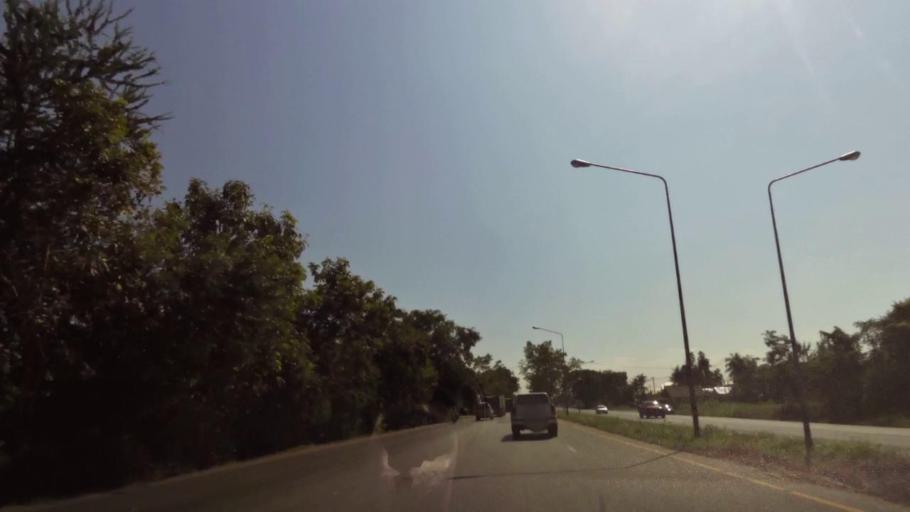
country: TH
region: Nakhon Sawan
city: Kao Liao
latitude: 15.8241
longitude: 100.1192
